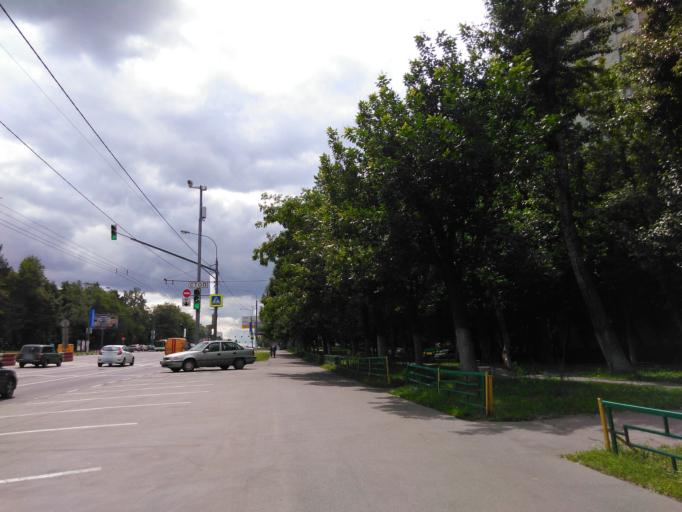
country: RU
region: Moscow
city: Zyuzino
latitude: 55.6597
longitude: 37.5741
